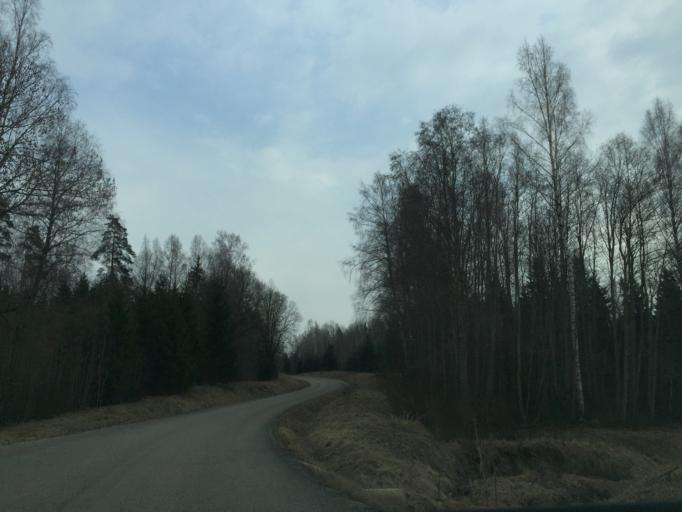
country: LV
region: Priekuli
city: Priekuli
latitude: 57.2159
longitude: 25.4054
